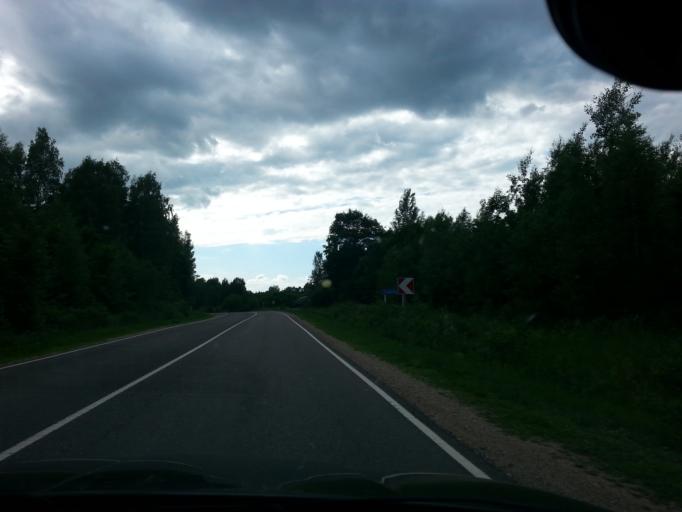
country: BY
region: Minsk
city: Svir
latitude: 54.8494
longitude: 26.2380
